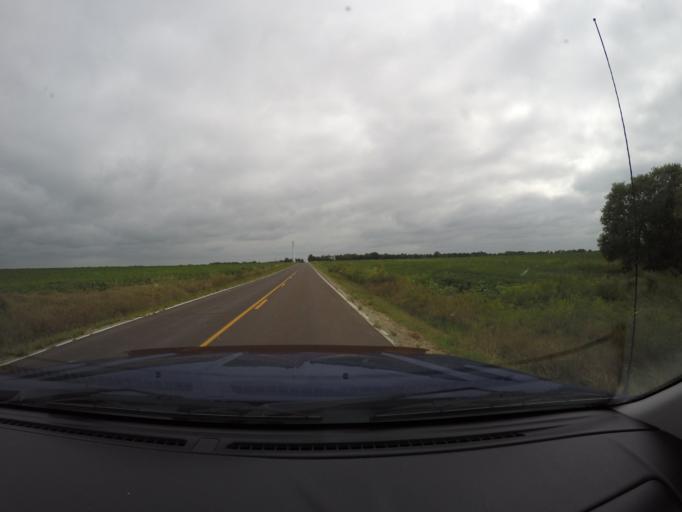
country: US
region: Kansas
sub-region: Morris County
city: Council Grove
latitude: 38.8542
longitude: -96.5939
